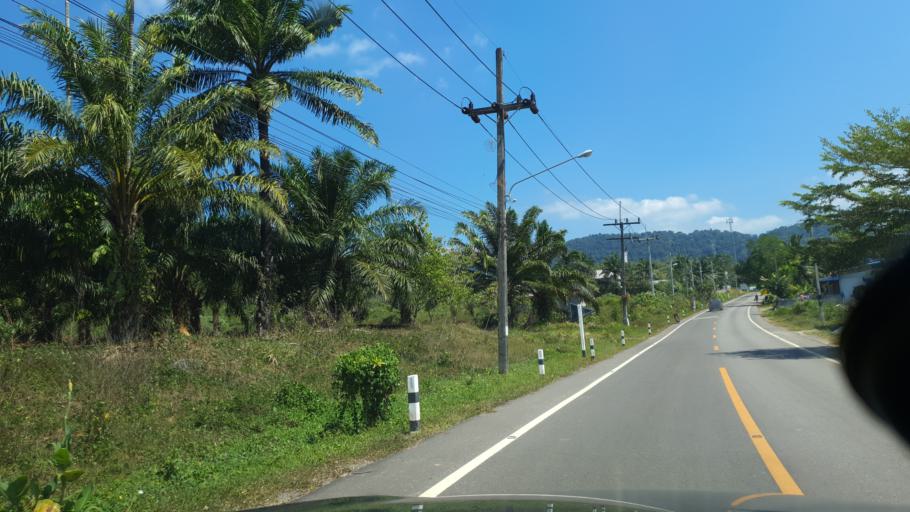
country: TH
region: Krabi
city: Khlong Thom
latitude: 7.9209
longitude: 99.2568
